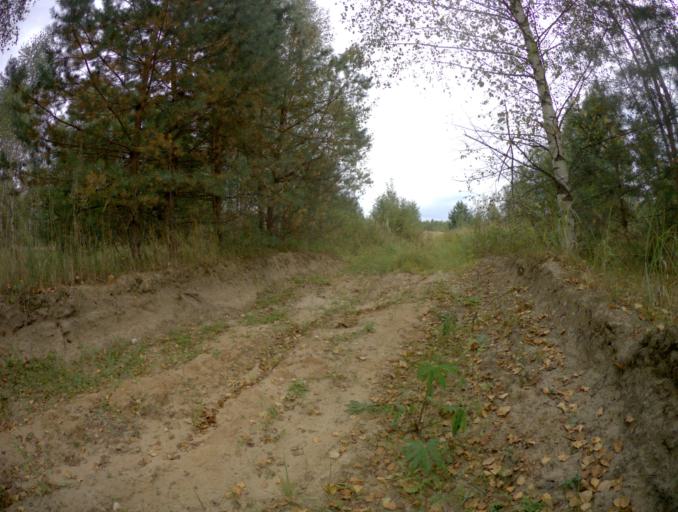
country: RU
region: Vladimir
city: Urshel'skiy
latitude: 55.8538
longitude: 40.2084
